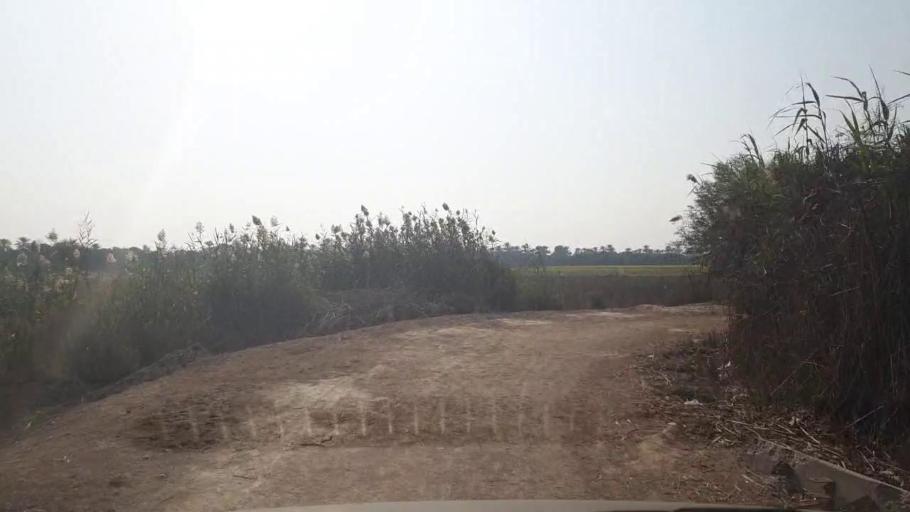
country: PK
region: Sindh
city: Tando Adam
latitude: 25.7991
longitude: 68.5915
